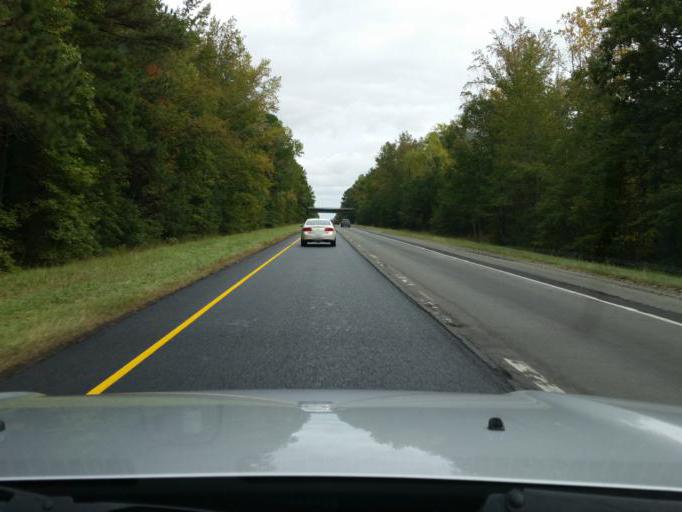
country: US
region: Virginia
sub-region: New Kent County
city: New Kent
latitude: 37.5088
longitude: -77.1307
